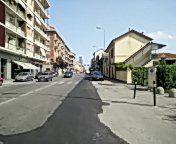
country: IT
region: Piedmont
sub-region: Provincia di Torino
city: Nichelino
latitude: 45.0073
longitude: 7.6576
